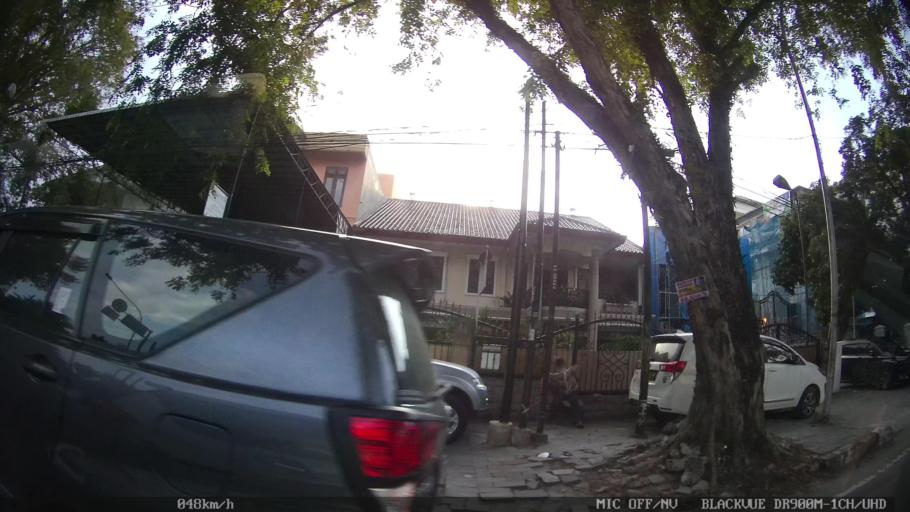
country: ID
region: North Sumatra
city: Medan
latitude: 3.5802
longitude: 98.6672
